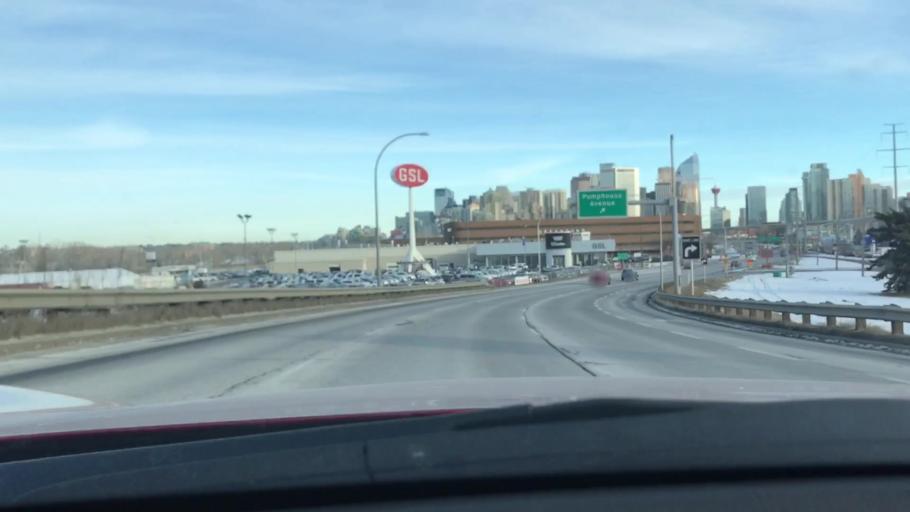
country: CA
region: Alberta
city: Calgary
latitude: 51.0458
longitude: -114.1047
